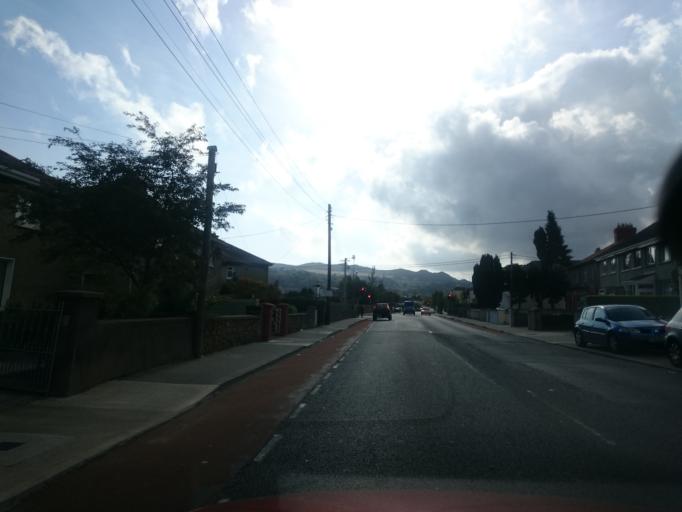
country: IE
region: Leinster
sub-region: Wicklow
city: Bray
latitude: 53.1936
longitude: -6.1064
